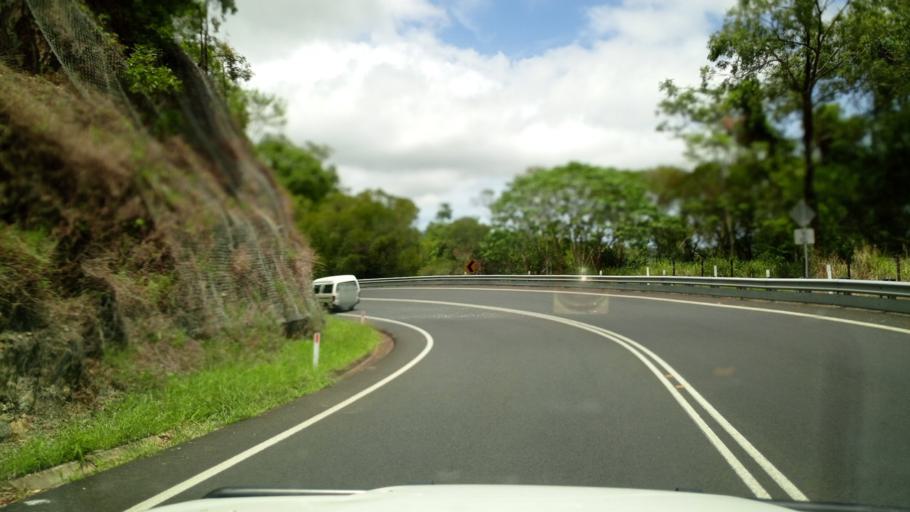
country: AU
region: Queensland
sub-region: Cairns
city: Redlynch
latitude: -16.8445
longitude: 145.6827
